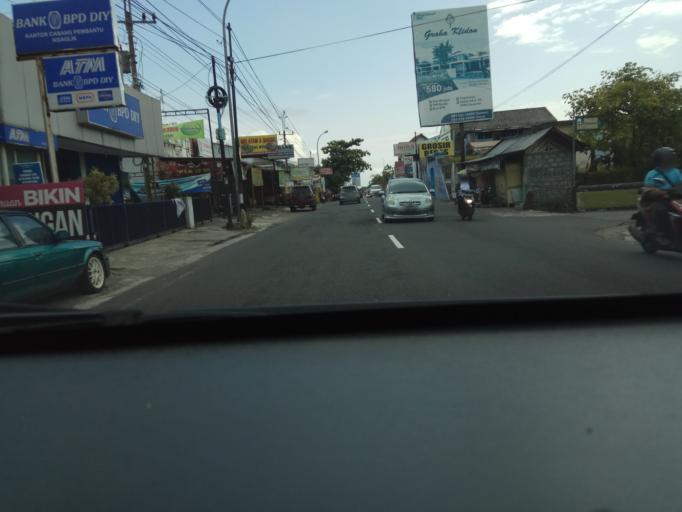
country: ID
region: Daerah Istimewa Yogyakarta
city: Melati
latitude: -7.7184
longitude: 110.4047
